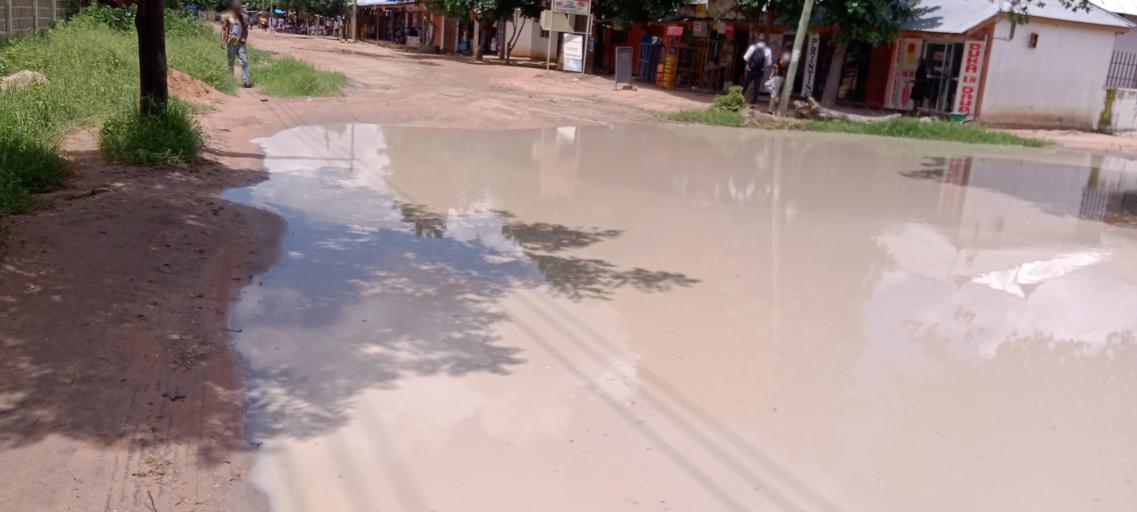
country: TZ
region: Dodoma
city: Dodoma
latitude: -6.1190
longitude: 35.7444
